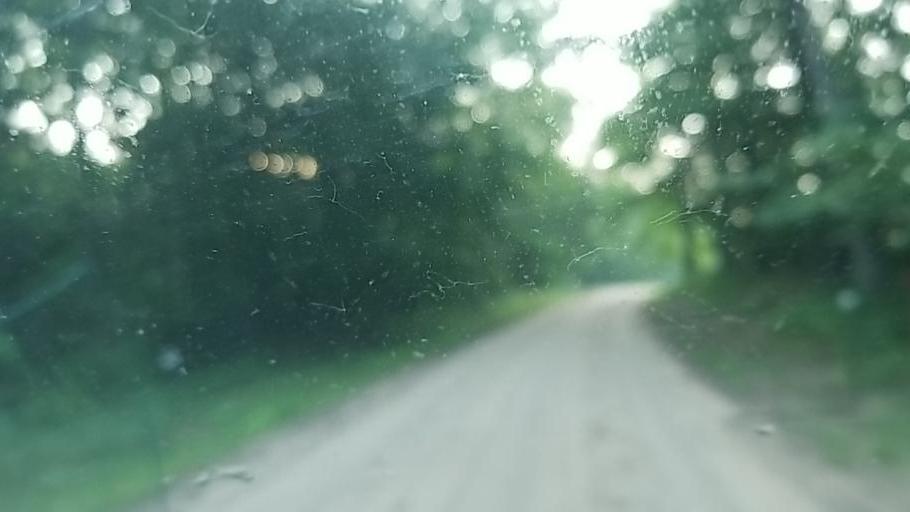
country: US
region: Michigan
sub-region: Muskegon County
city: Twin Lake
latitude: 43.4534
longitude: -86.0931
